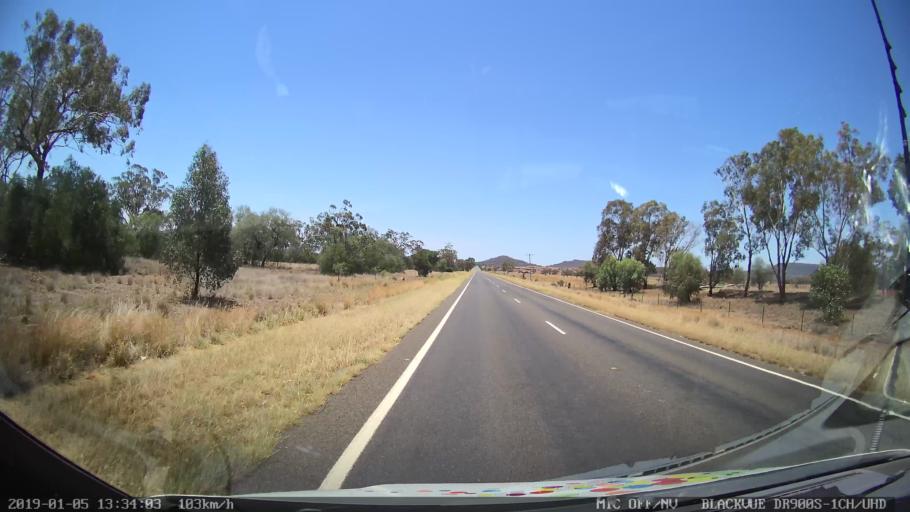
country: AU
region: New South Wales
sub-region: Gunnedah
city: Gunnedah
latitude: -30.9976
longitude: 150.1266
